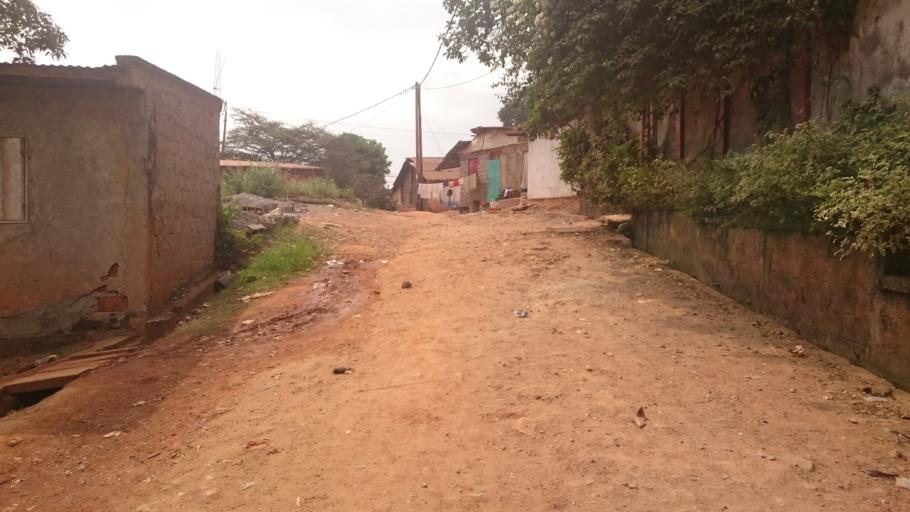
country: CM
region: Centre
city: Yaounde
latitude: 3.8183
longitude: 11.5044
